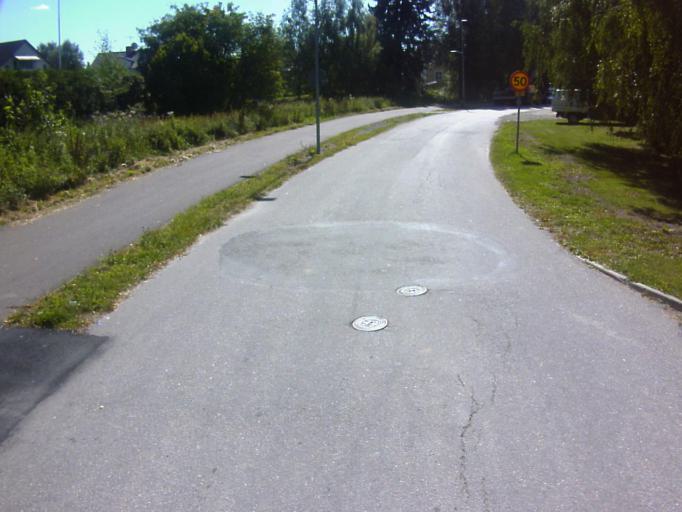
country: SE
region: Soedermanland
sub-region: Eskilstuna Kommun
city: Hallbybrunn
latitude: 59.3766
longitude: 16.4548
